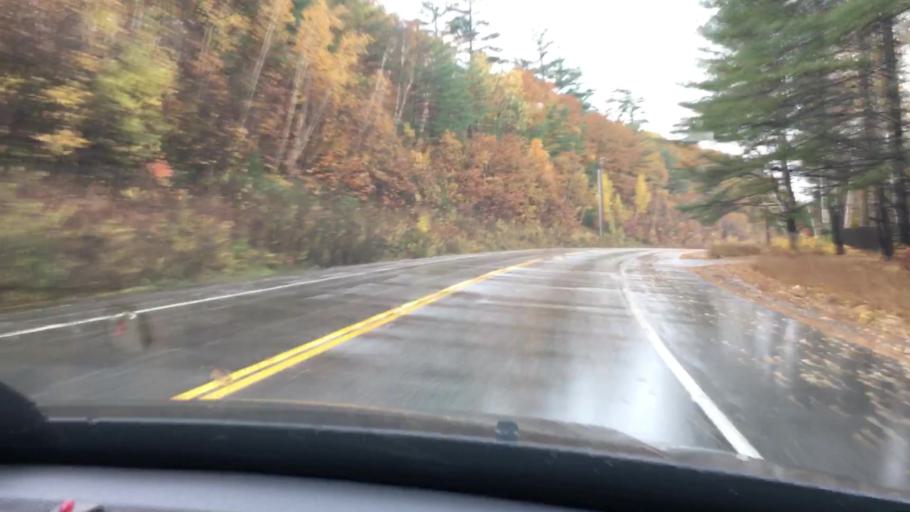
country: US
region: New Hampshire
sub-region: Grafton County
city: Holderness
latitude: 43.7311
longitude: -71.5733
